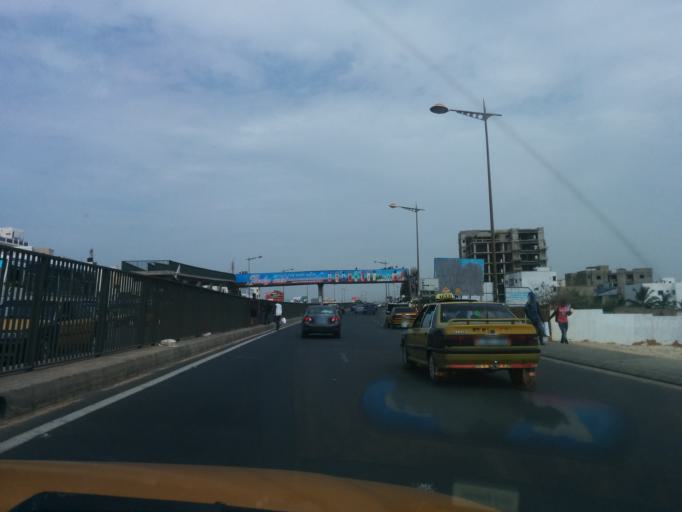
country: SN
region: Dakar
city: Grand Dakar
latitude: 14.7459
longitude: -17.4675
